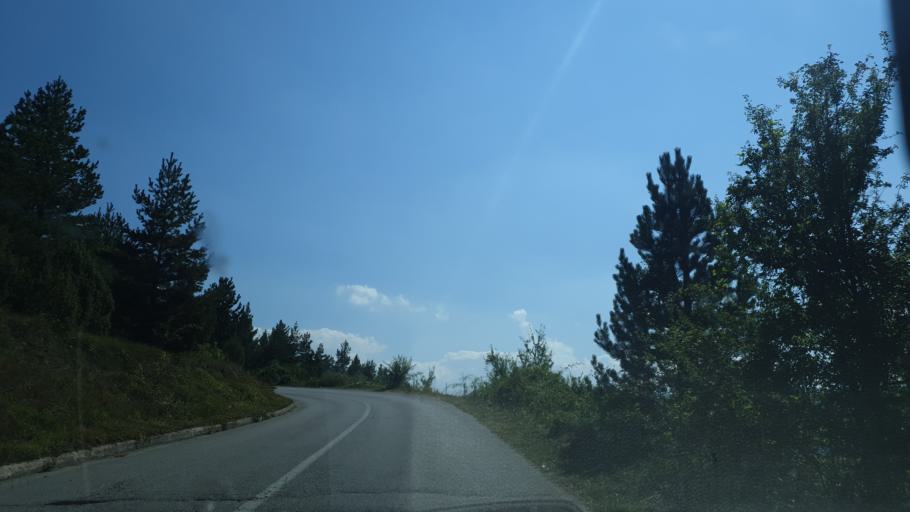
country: RS
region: Central Serbia
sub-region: Zlatiborski Okrug
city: Cajetina
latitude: 43.6752
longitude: 19.8377
